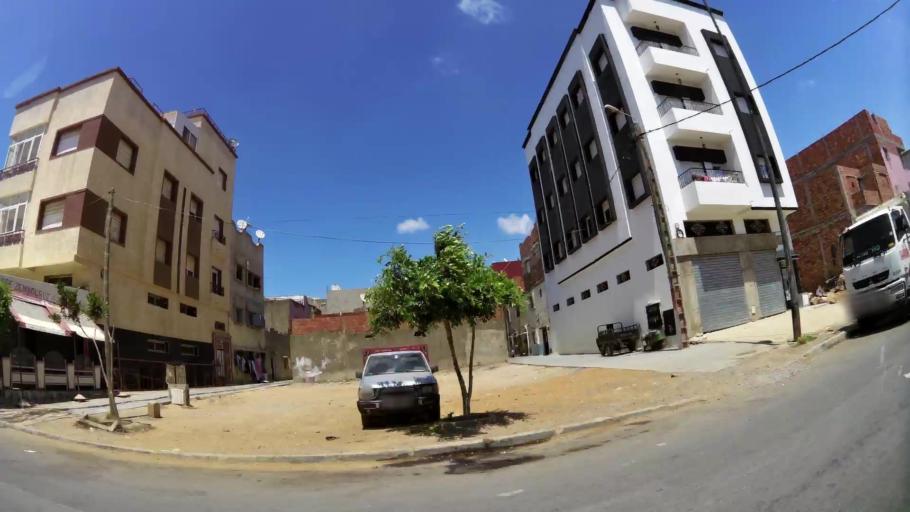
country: MA
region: Gharb-Chrarda-Beni Hssen
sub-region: Kenitra Province
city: Kenitra
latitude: 34.2566
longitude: -6.5473
